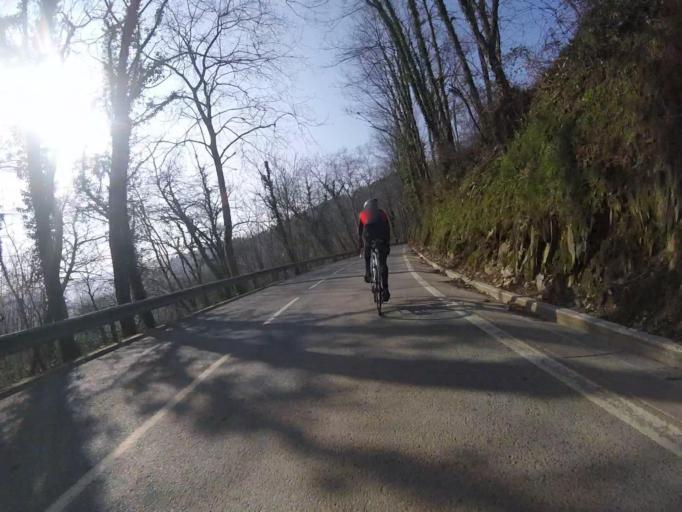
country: ES
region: Navarre
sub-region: Provincia de Navarra
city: Bera
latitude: 43.2963
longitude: -1.6899
